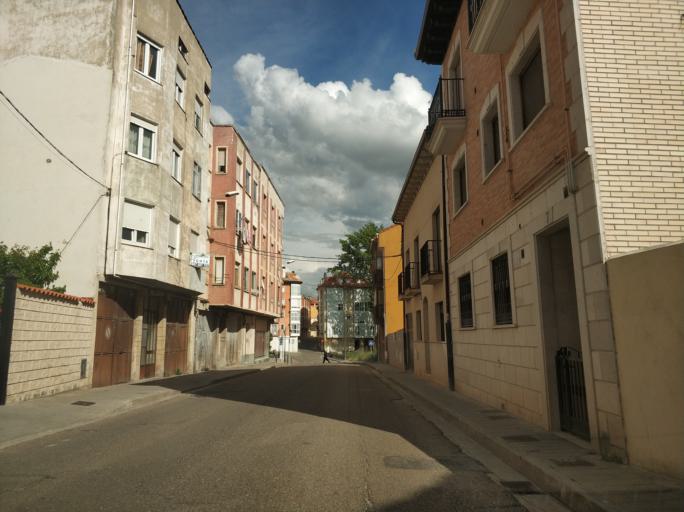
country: ES
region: Castille and Leon
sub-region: Provincia de Burgos
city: Aranda de Duero
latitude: 41.6723
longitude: -3.6924
